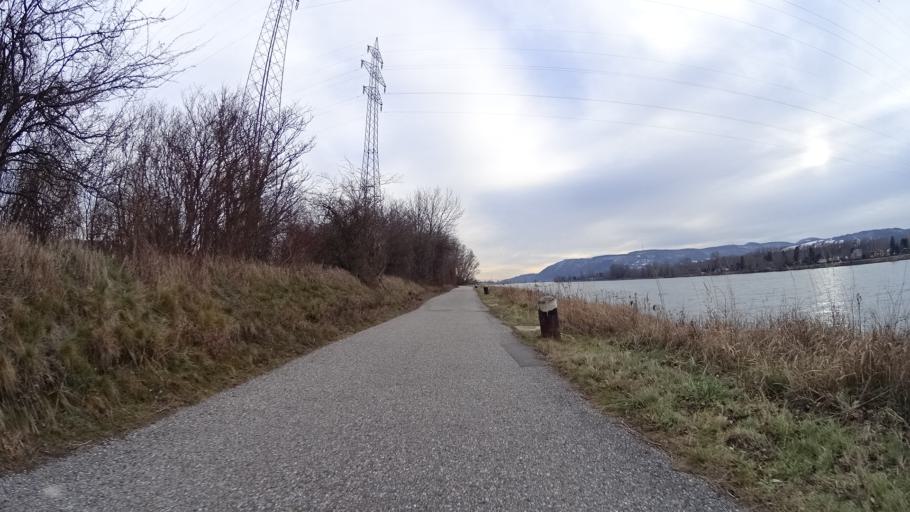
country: AT
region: Lower Austria
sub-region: Politischer Bezirk Korneuburg
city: Bisamberg
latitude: 48.3257
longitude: 16.3353
